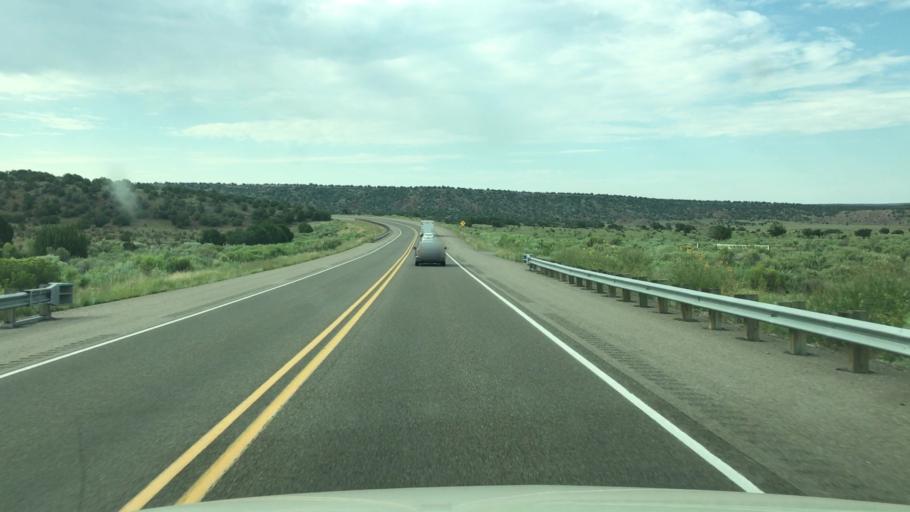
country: US
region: New Mexico
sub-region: Santa Fe County
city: Eldorado at Santa Fe
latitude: 35.2851
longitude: -105.8231
